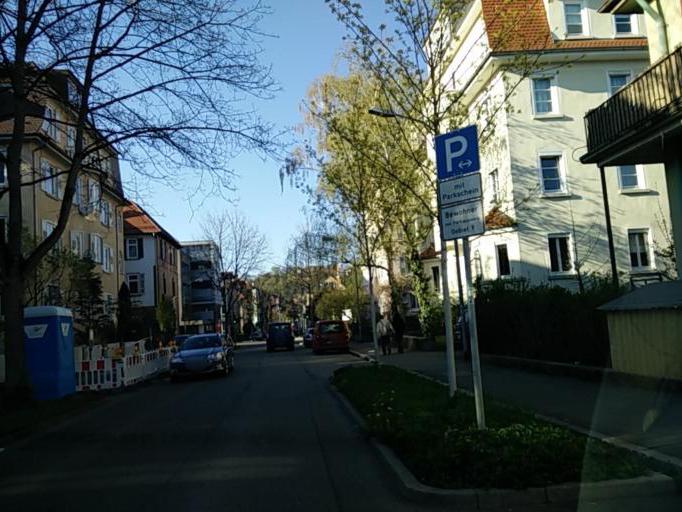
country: DE
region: Baden-Wuerttemberg
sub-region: Tuebingen Region
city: Tuebingen
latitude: 48.5132
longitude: 9.0602
